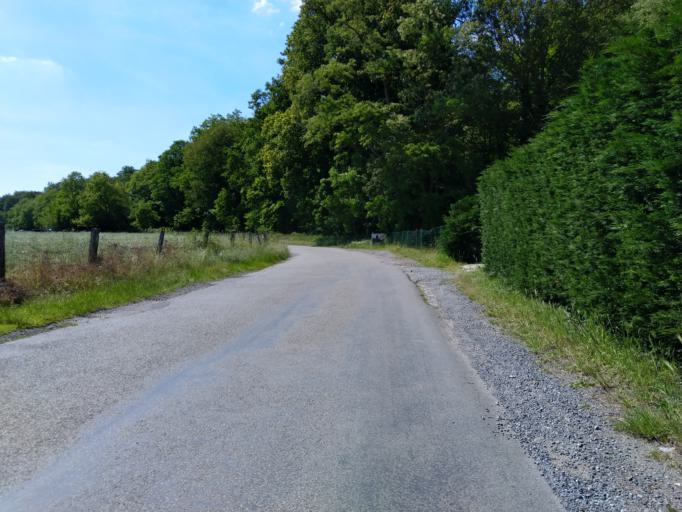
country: BE
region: Wallonia
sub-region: Province du Hainaut
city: Jurbise
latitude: 50.4913
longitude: 3.9183
